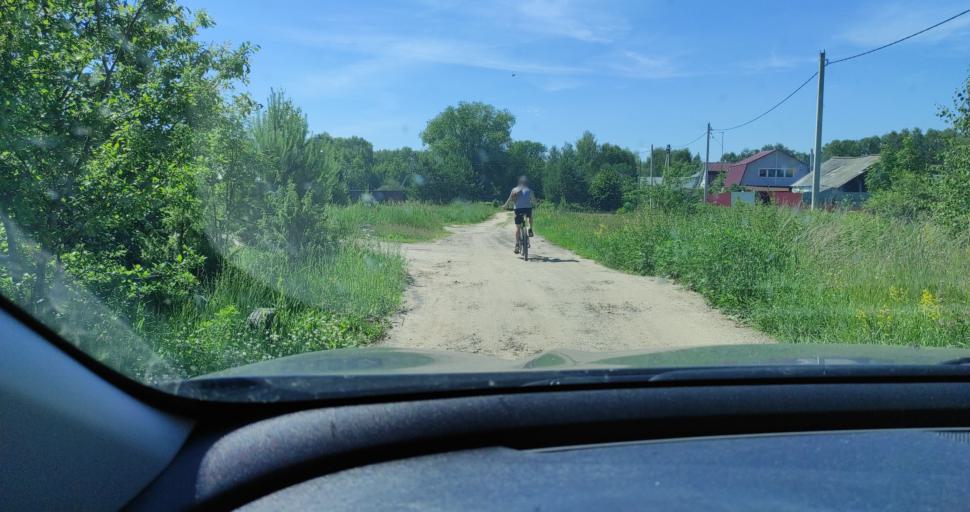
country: RU
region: Rjazan
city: Murmino
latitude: 54.5605
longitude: 40.0940
